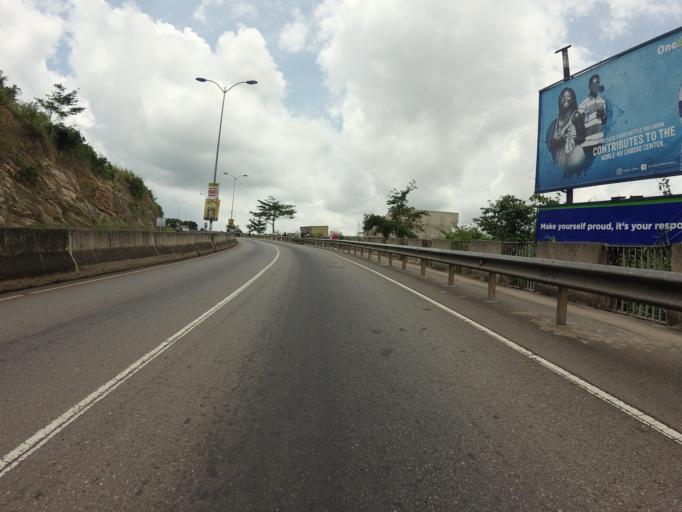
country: GH
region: Eastern
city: Aburi
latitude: 5.7957
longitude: -0.1833
